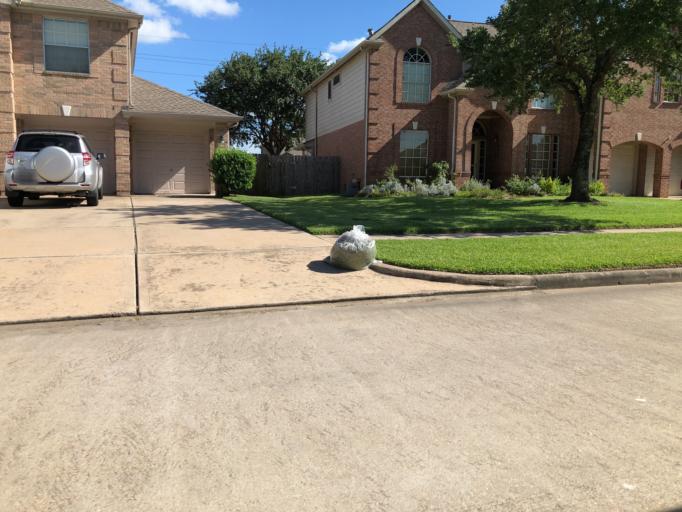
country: US
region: Texas
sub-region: Harris County
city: Katy
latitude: 29.8056
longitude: -95.8297
